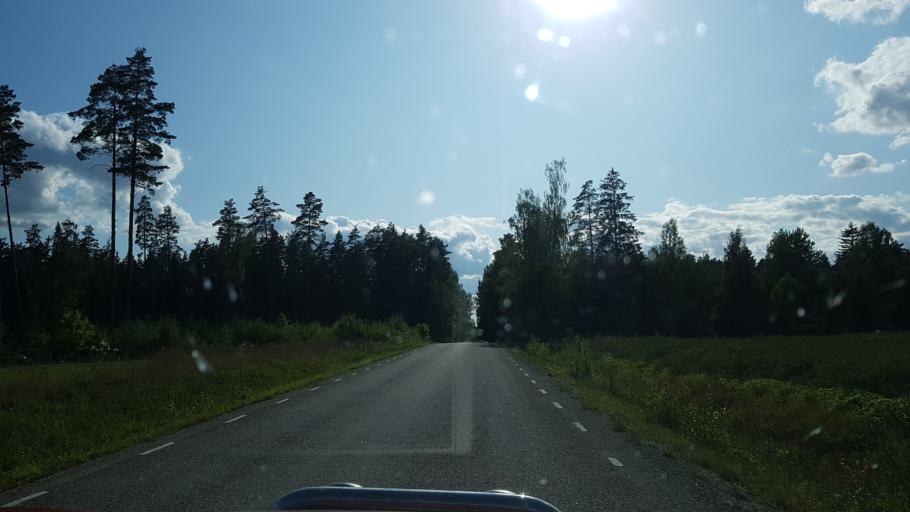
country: EE
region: Vorumaa
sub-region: Voru linn
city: Voru
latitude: 57.9246
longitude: 27.0414
